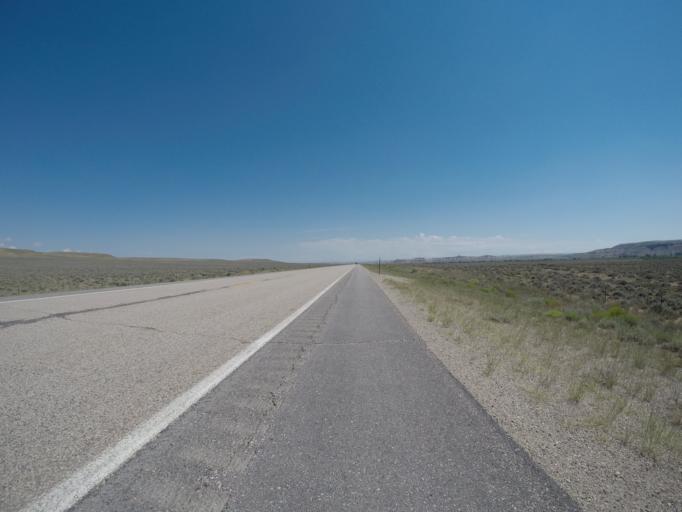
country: US
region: Wyoming
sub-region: Sublette County
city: Marbleton
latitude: 42.4338
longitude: -110.1037
